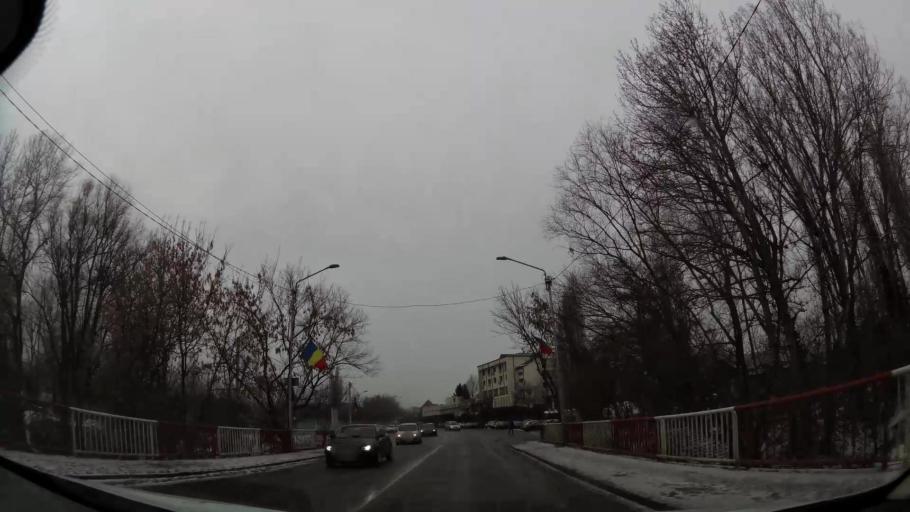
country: RO
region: Dambovita
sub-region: Municipiul Targoviste
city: Targoviste
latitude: 44.9379
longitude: 25.4562
